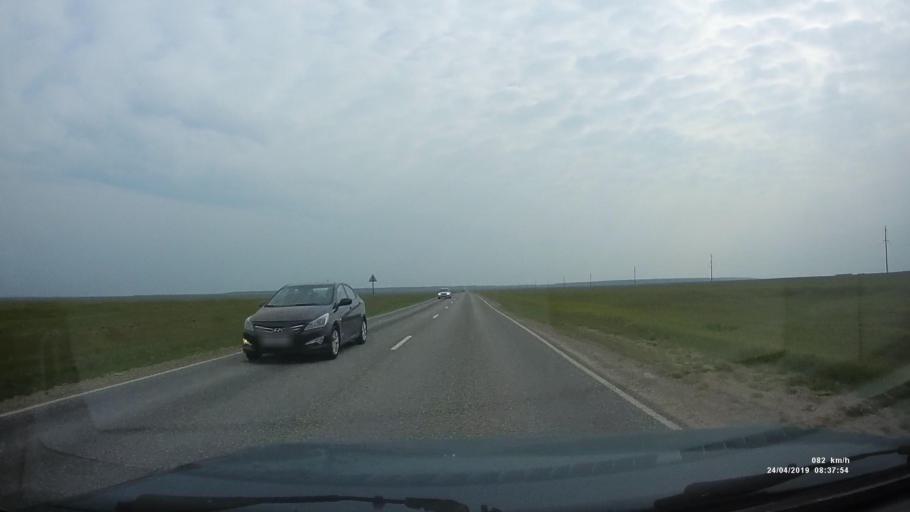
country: RU
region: Kalmykiya
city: Arshan'
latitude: 46.2124
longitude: 43.9581
